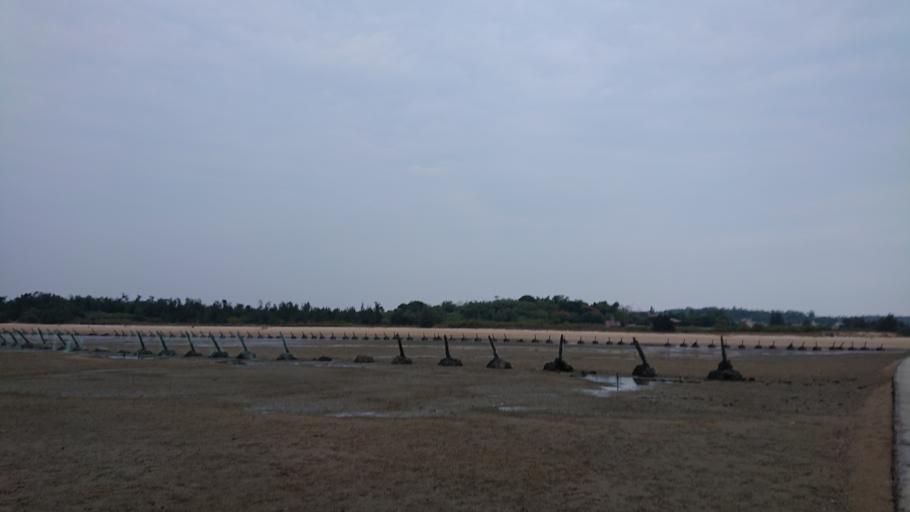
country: TW
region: Fukien
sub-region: Kinmen
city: Jincheng
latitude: 24.4306
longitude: 118.2251
